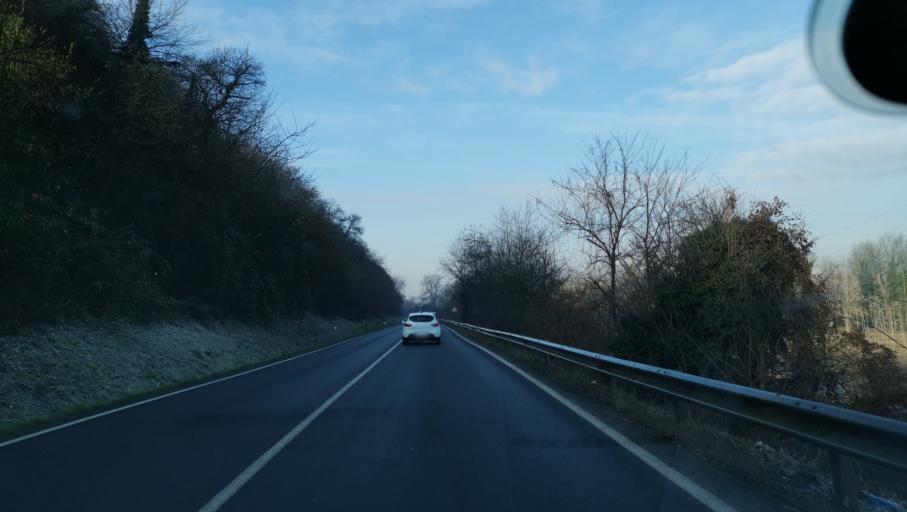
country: IT
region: Piedmont
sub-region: Provincia di Torino
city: Chivasso
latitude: 45.1757
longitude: 7.9190
